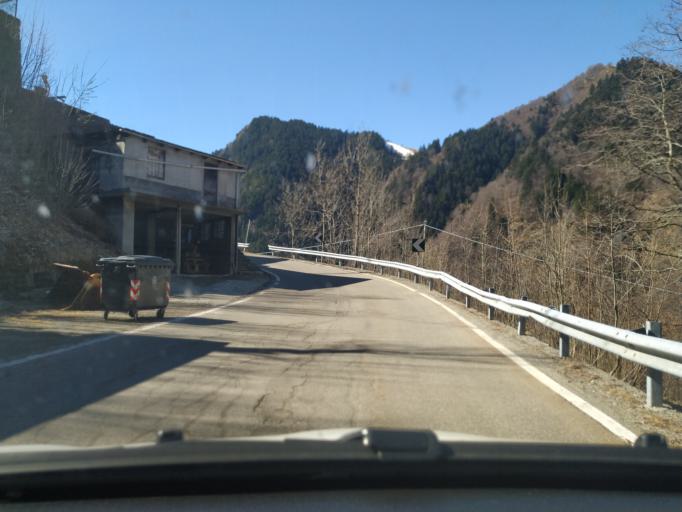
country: IT
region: Piedmont
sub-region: Provincia di Vercelli
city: Rimella
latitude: 45.9087
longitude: 8.1813
